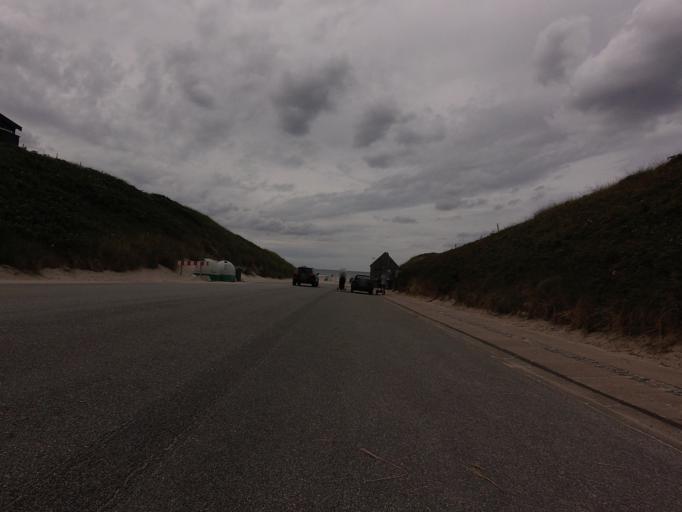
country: DK
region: North Denmark
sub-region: Jammerbugt Kommune
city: Pandrup
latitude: 57.3623
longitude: 9.7006
